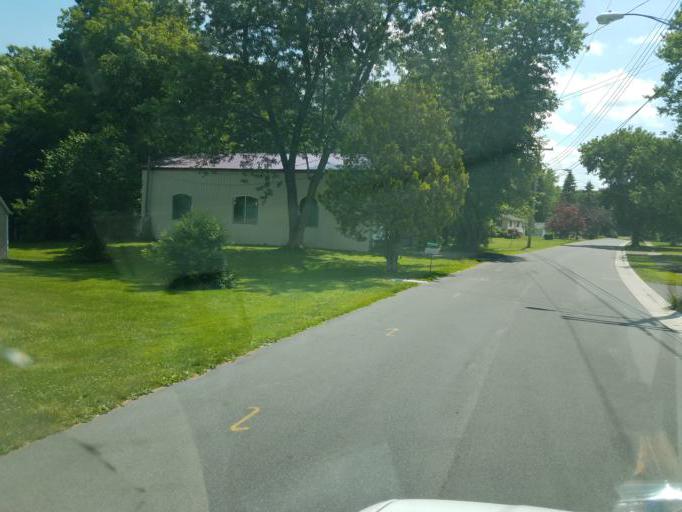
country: US
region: New York
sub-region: Wayne County
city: Clyde
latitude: 43.0782
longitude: -76.8670
